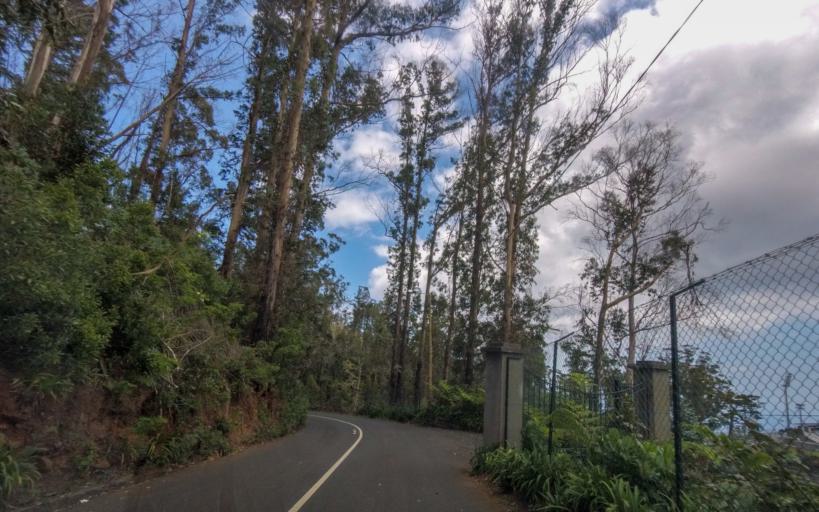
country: PT
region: Madeira
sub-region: Funchal
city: Nossa Senhora do Monte
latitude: 32.6738
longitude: -16.8842
